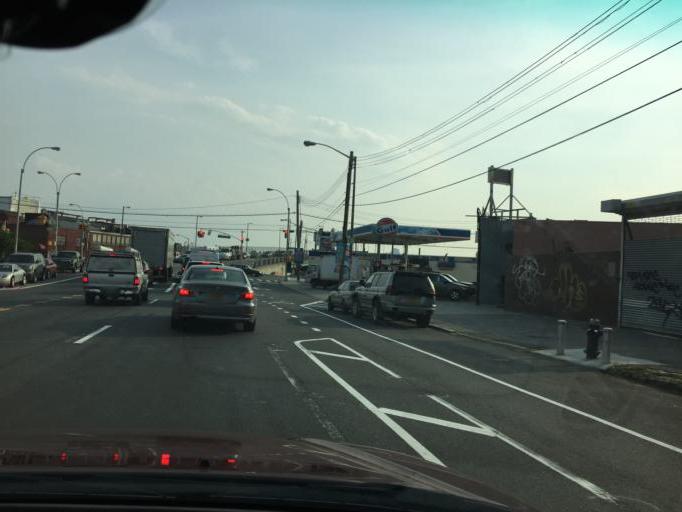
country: US
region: New York
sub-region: Queens County
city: Long Island City
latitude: 40.7350
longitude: -73.9376
